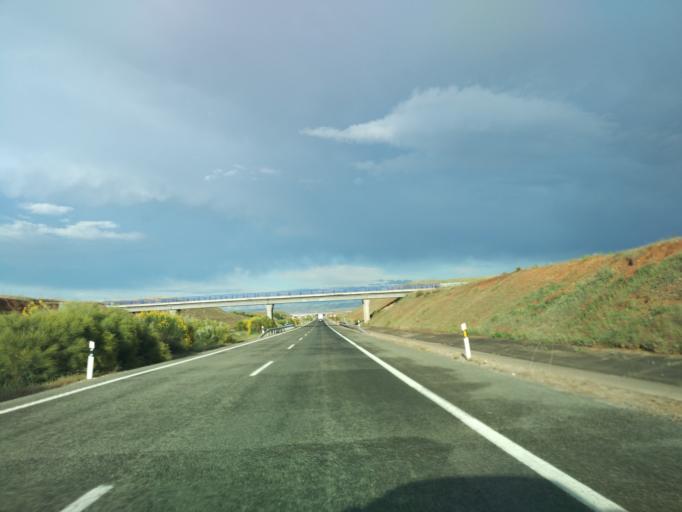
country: ES
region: Madrid
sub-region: Provincia de Madrid
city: Ajalvir
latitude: 40.5059
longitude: -3.4620
